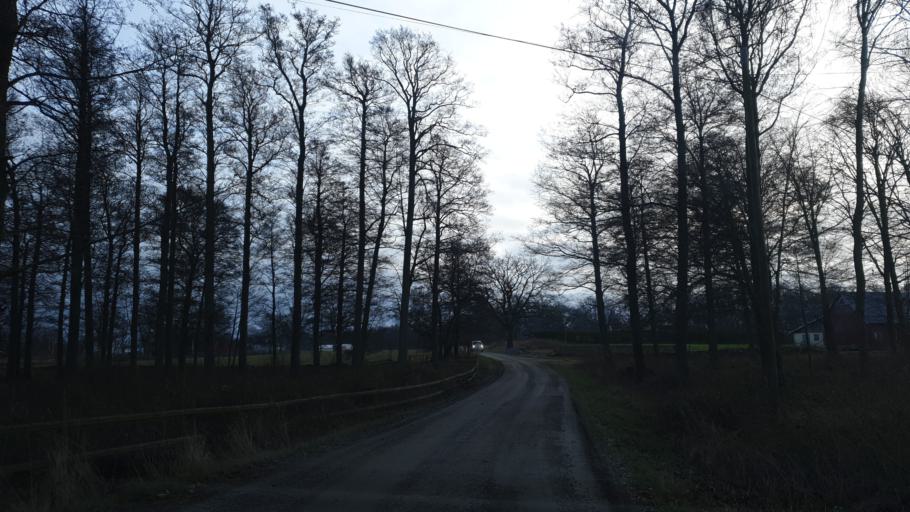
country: SE
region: Kalmar
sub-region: Torsas Kommun
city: Torsas
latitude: 56.3098
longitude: 16.0413
